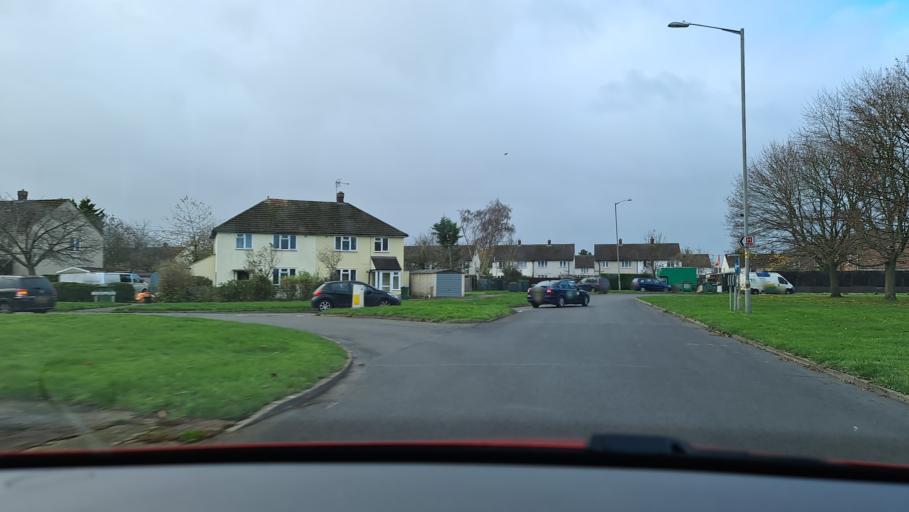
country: GB
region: England
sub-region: Buckinghamshire
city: Aylesbury
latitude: 51.8033
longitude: -0.8161
